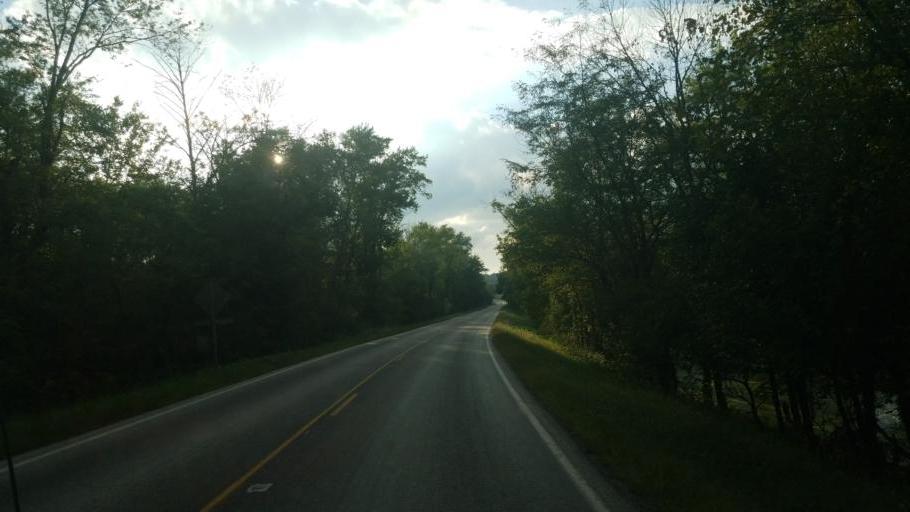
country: US
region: Ohio
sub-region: Wayne County
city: Shreve
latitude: 40.7488
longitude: -82.1308
